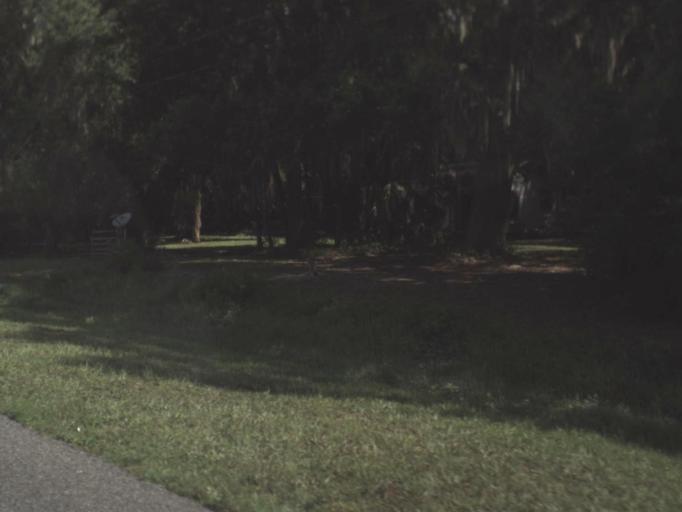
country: US
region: Florida
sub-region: Alachua County
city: Gainesville
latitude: 29.4976
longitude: -82.2597
